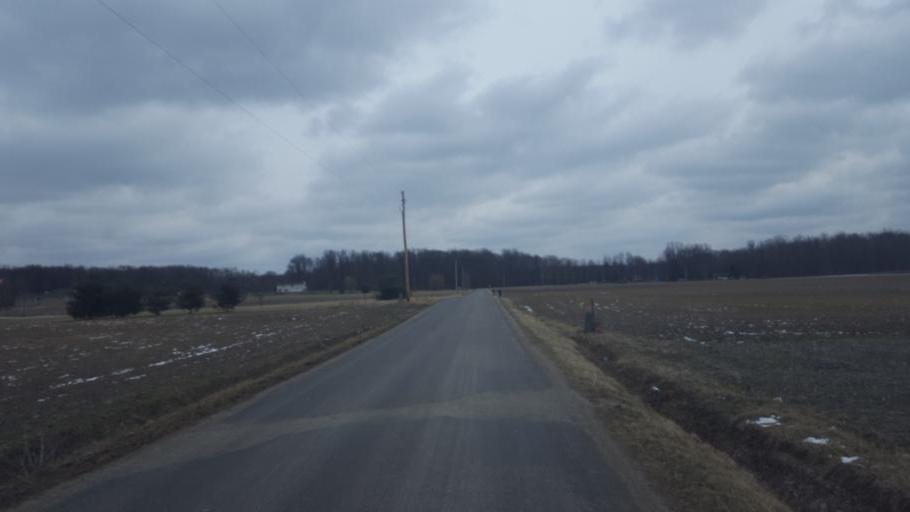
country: US
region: Ohio
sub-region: Crawford County
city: Crestline
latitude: 40.7502
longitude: -82.6944
